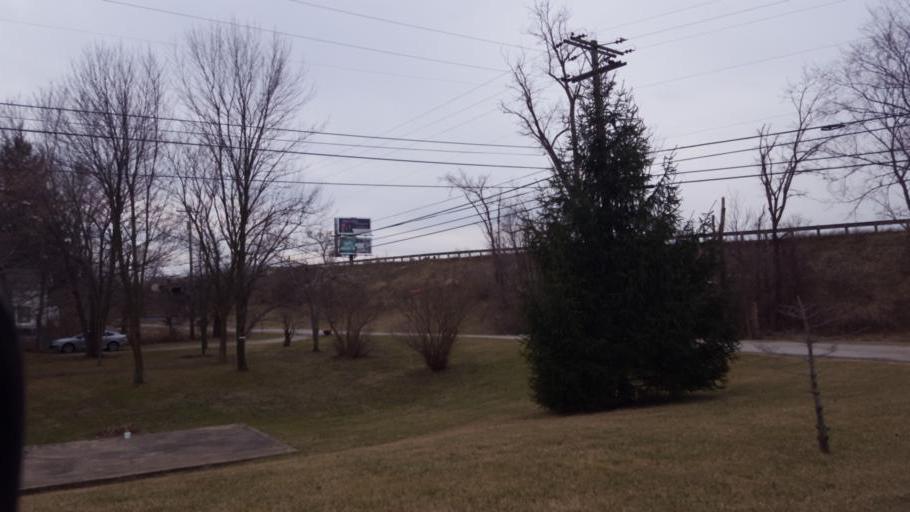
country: US
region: Ohio
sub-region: Richland County
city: Ontario
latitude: 40.8138
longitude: -82.5899
